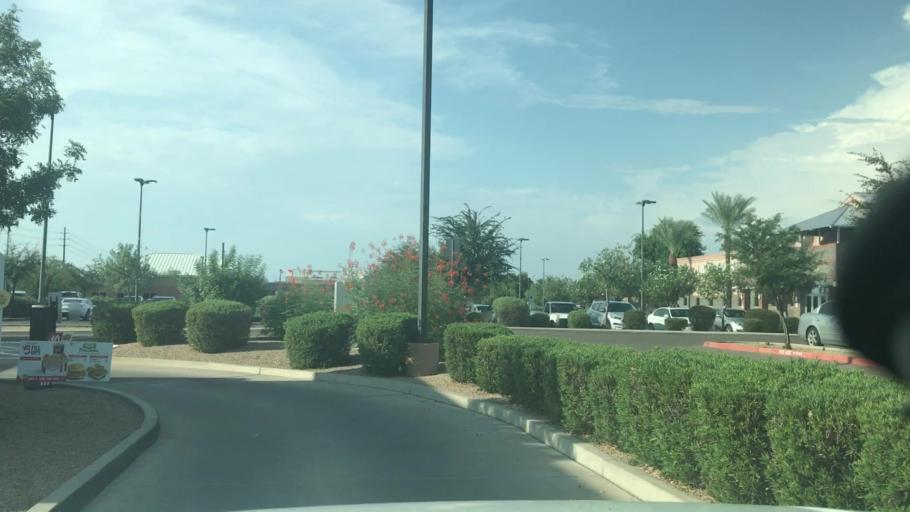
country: US
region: Arizona
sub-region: Maricopa County
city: Gilbert
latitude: 33.3480
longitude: -111.7548
